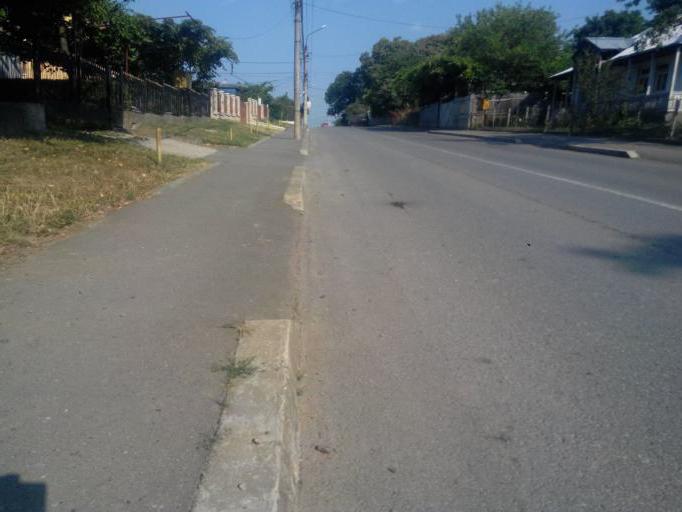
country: RO
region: Suceava
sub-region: Municipiul Falticeni
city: Falticeni
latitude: 47.4651
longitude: 26.2881
